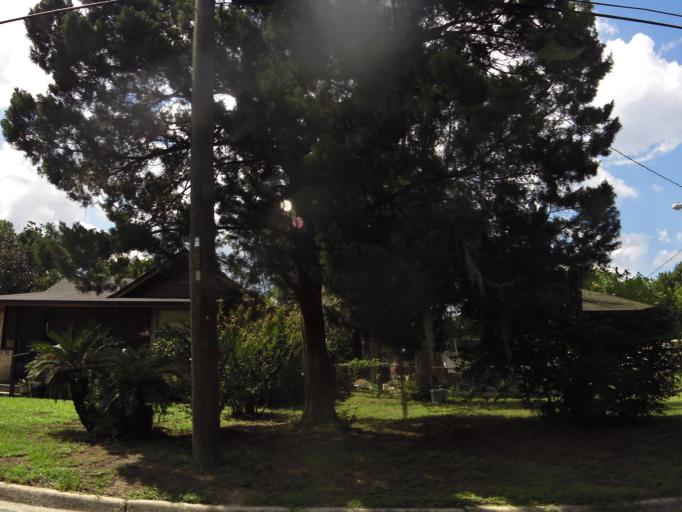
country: US
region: Florida
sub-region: Duval County
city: Jacksonville
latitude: 30.3836
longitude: -81.6516
